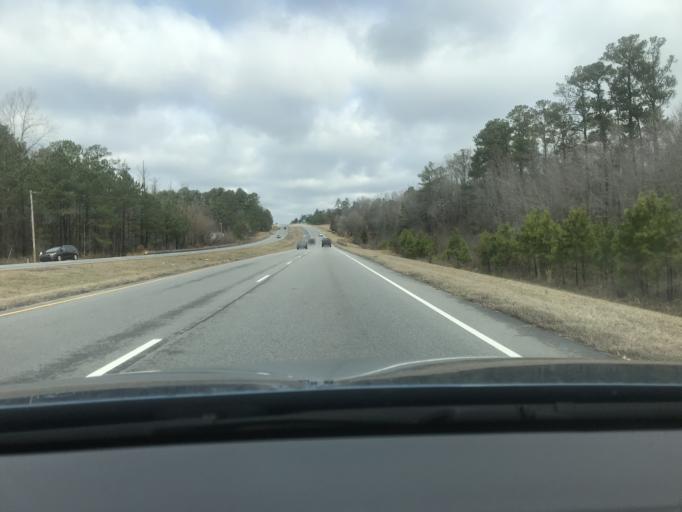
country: US
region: North Carolina
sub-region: Cumberland County
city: Spring Lake
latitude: 35.2848
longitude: -79.0750
